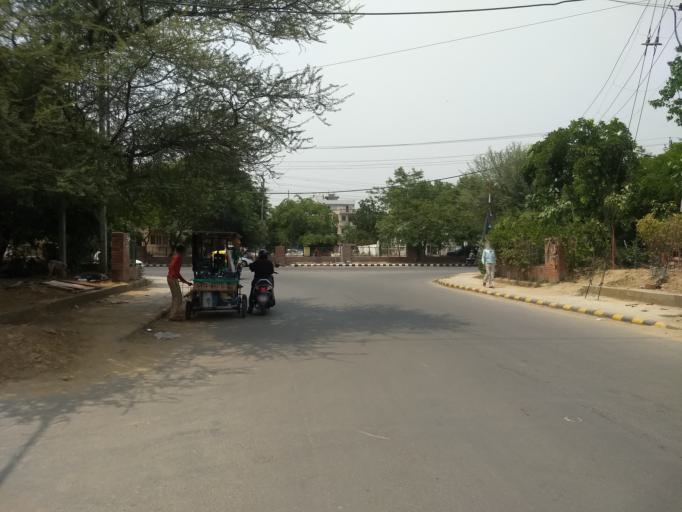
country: IN
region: Haryana
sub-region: Gurgaon
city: Gurgaon
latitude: 28.4623
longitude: 77.0925
